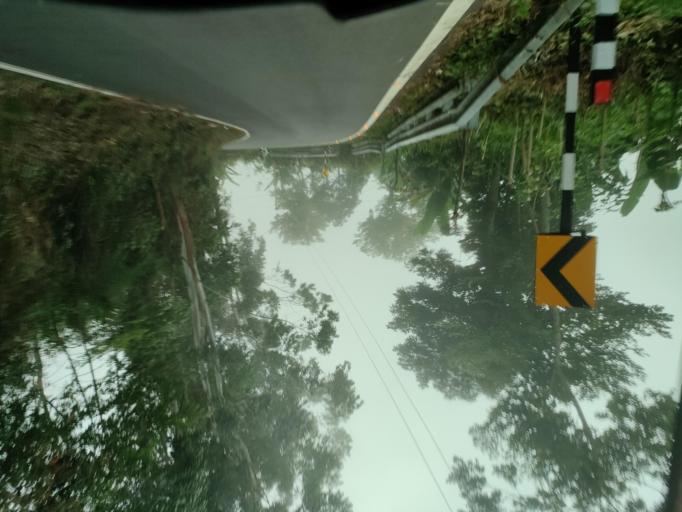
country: IN
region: Tamil Nadu
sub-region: Dindigul
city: Ayakudi
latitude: 10.3334
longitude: 77.5628
